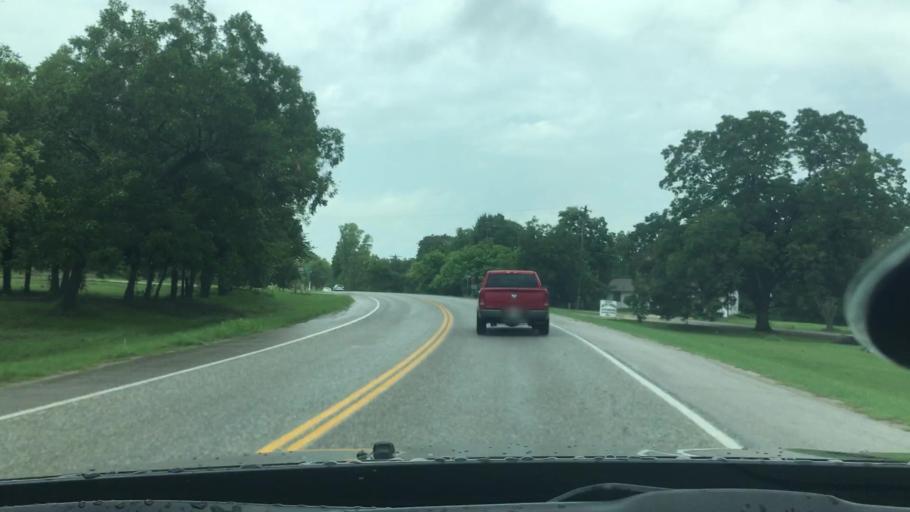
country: US
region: Oklahoma
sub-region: Johnston County
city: Tishomingo
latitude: 34.2440
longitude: -96.7522
